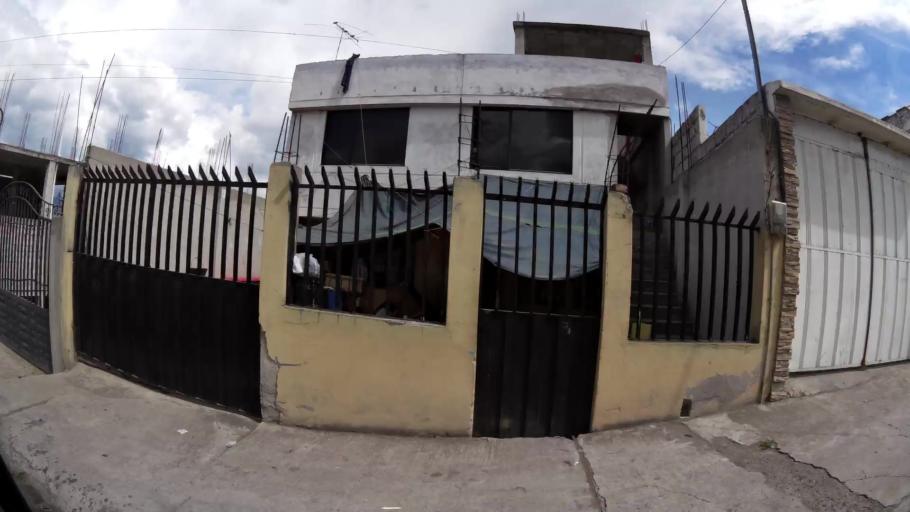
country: EC
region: Tungurahua
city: Ambato
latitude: -1.2592
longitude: -78.6183
